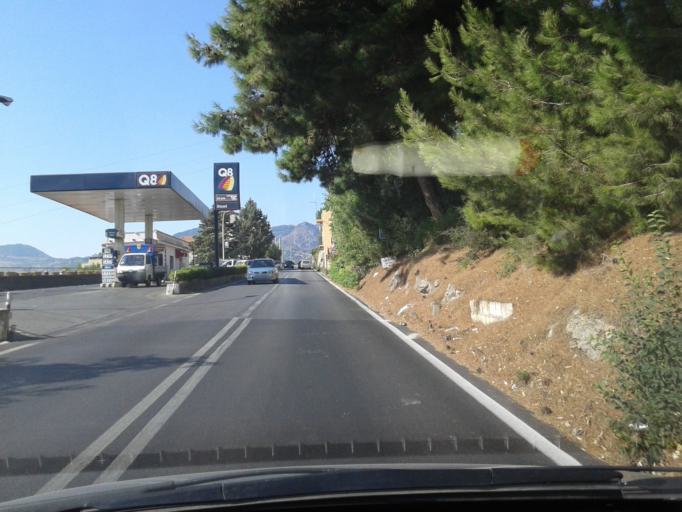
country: IT
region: Sicily
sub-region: Palermo
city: Cannizzaro-Favara
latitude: 38.0651
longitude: 13.2669
